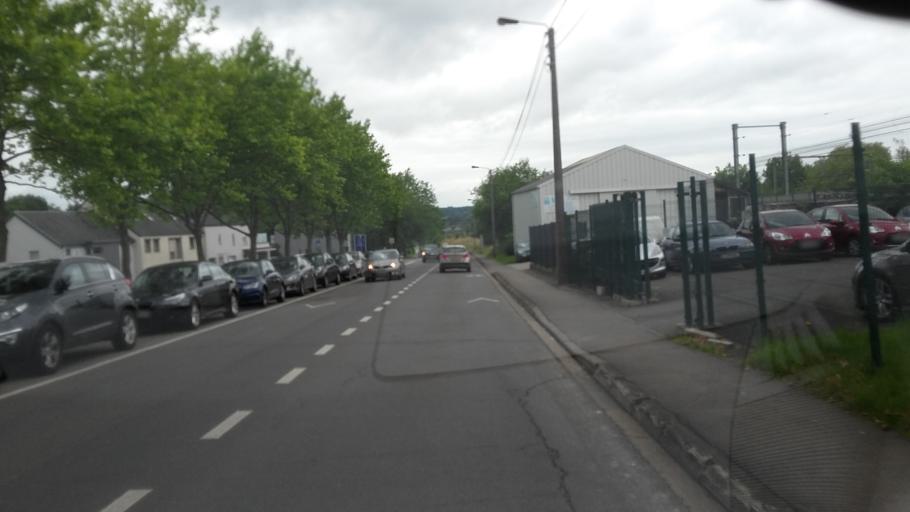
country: BE
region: Wallonia
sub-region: Province du Luxembourg
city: Arlon
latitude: 49.6814
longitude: 5.8029
